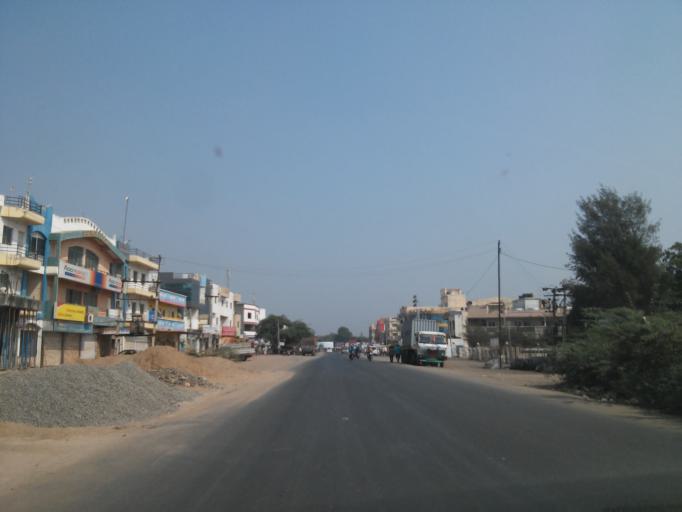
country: IN
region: Gujarat
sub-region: Kachchh
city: Mundra
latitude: 22.8389
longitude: 69.7054
